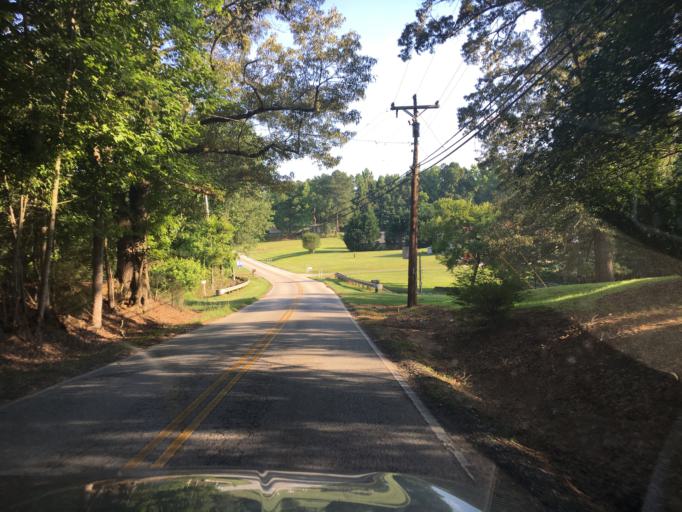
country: US
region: South Carolina
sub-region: Spartanburg County
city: Duncan
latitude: 34.8587
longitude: -82.1102
